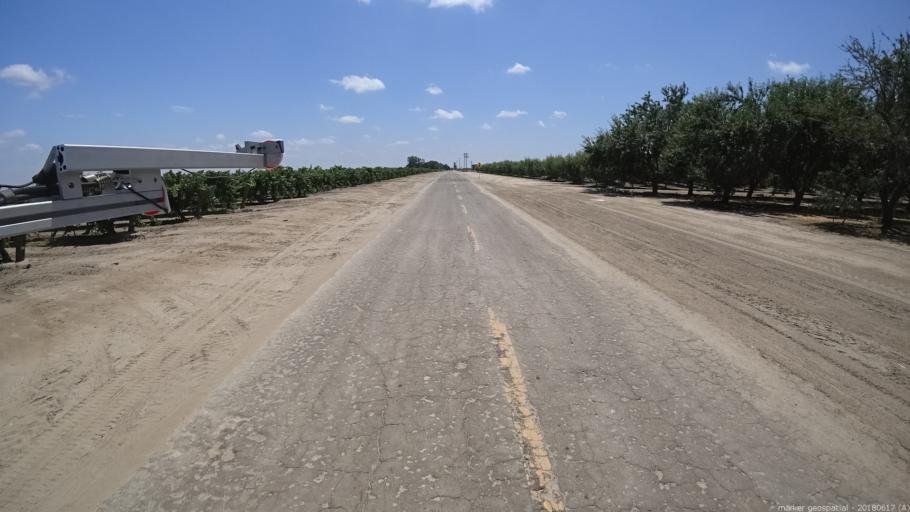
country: US
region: California
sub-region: Fresno County
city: Biola
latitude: 36.8243
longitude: -120.1329
